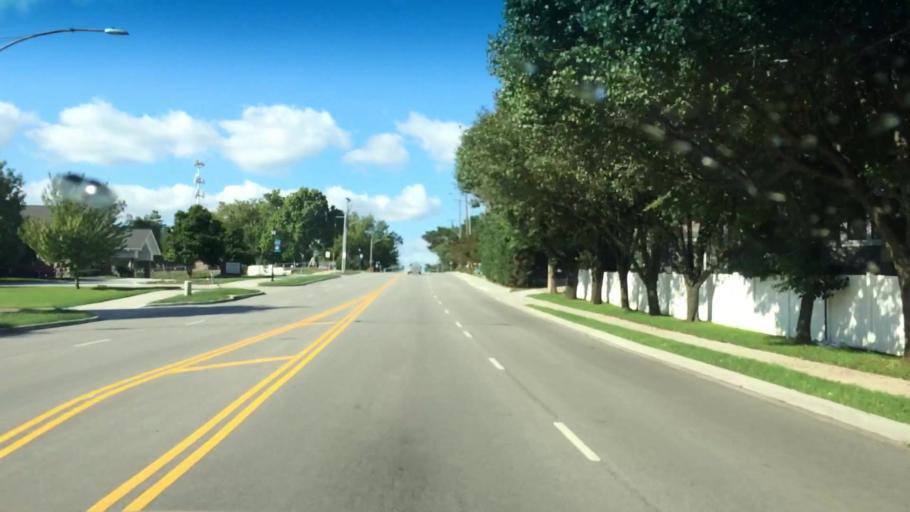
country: US
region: Kansas
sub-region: Johnson County
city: Prairie Village
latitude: 38.9865
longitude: -94.6304
